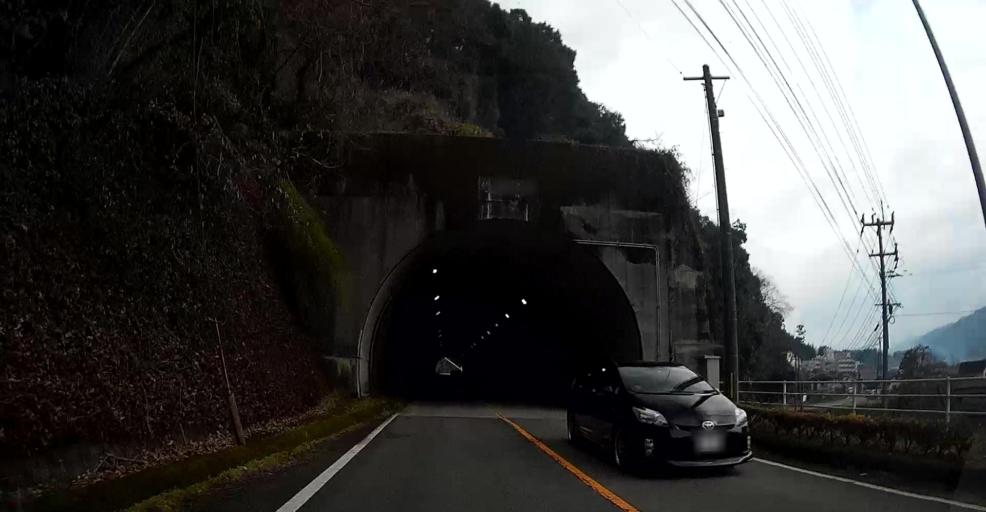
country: JP
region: Kumamoto
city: Matsubase
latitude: 32.6171
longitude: 130.8544
